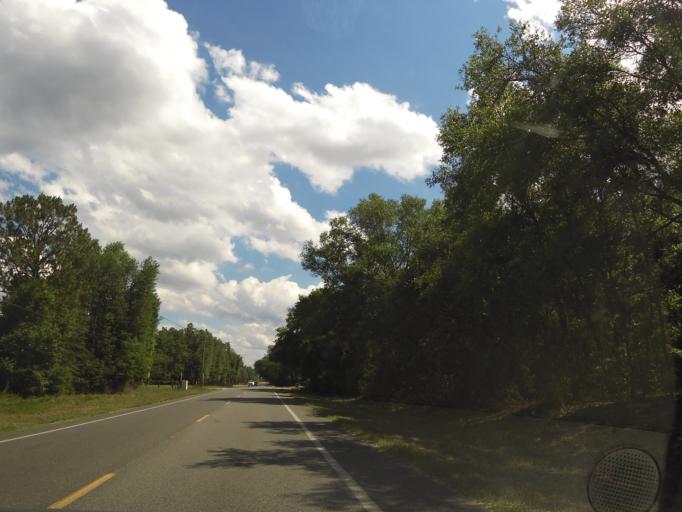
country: US
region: Florida
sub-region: Clay County
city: Keystone Heights
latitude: 29.8284
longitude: -81.9225
